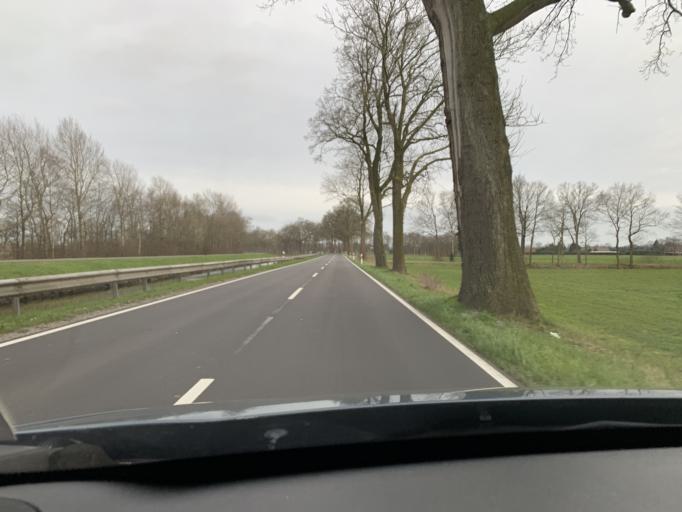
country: DE
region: Lower Saxony
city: Apen
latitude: 53.2053
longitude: 7.7572
